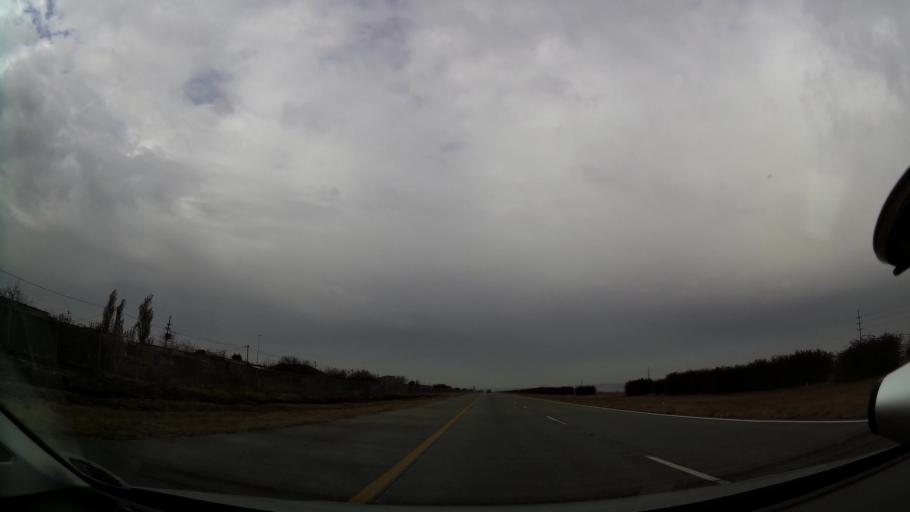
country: ZA
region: Gauteng
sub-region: City of Johannesburg Metropolitan Municipality
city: Orange Farm
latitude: -26.5112
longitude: 27.8120
